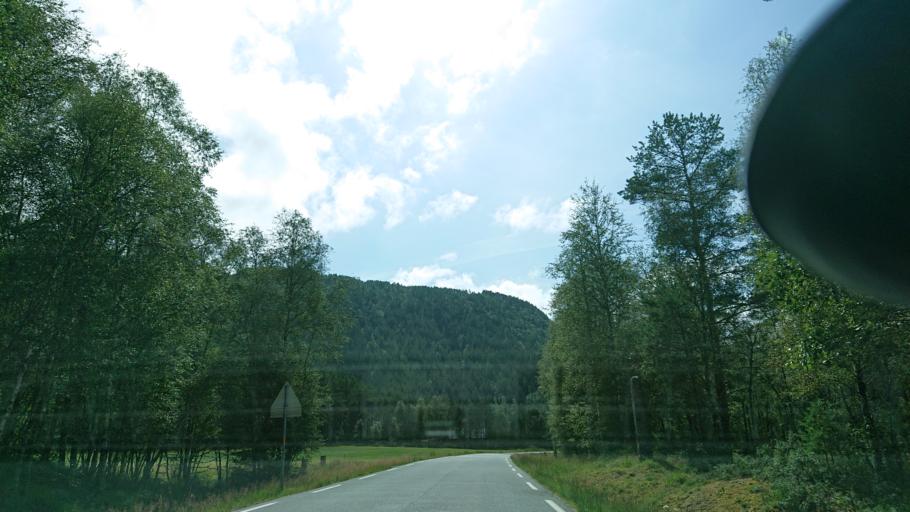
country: NO
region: Rogaland
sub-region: Hjelmeland
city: Hjelmelandsvagen
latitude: 59.2397
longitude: 6.2763
